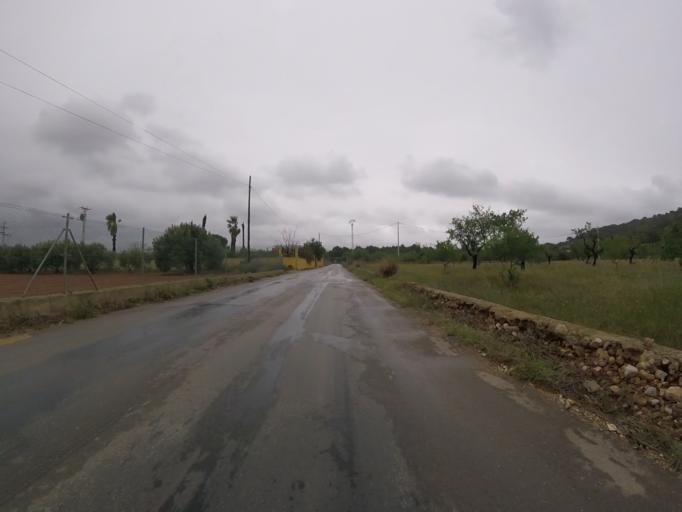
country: ES
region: Valencia
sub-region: Provincia de Castello
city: Alcoceber
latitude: 40.2476
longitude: 0.2464
